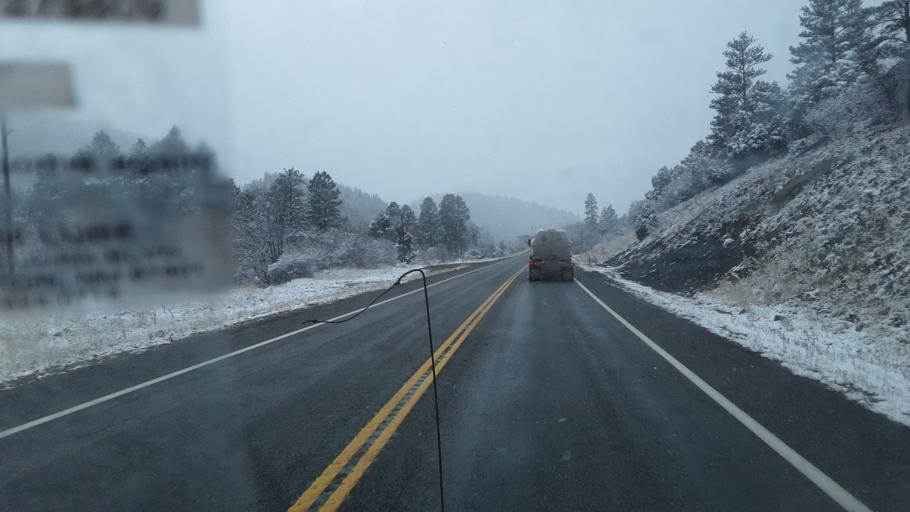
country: US
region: Colorado
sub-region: La Plata County
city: Bayfield
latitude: 37.2289
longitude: -107.3814
